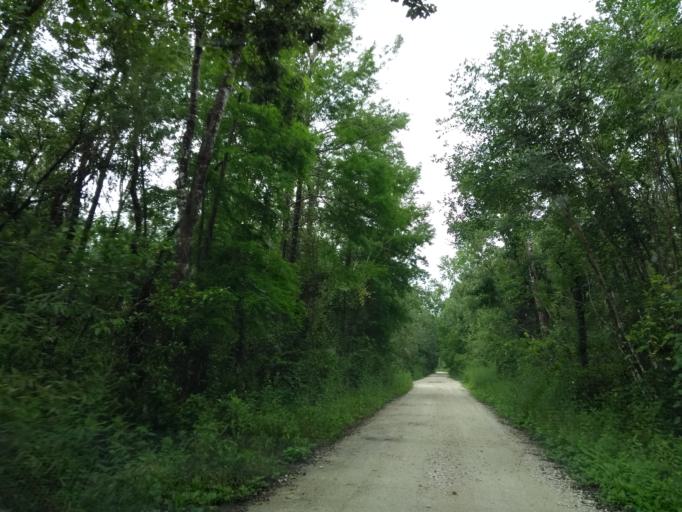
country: US
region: Florida
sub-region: Collier County
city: Lely Resort
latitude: 25.9845
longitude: -81.4110
